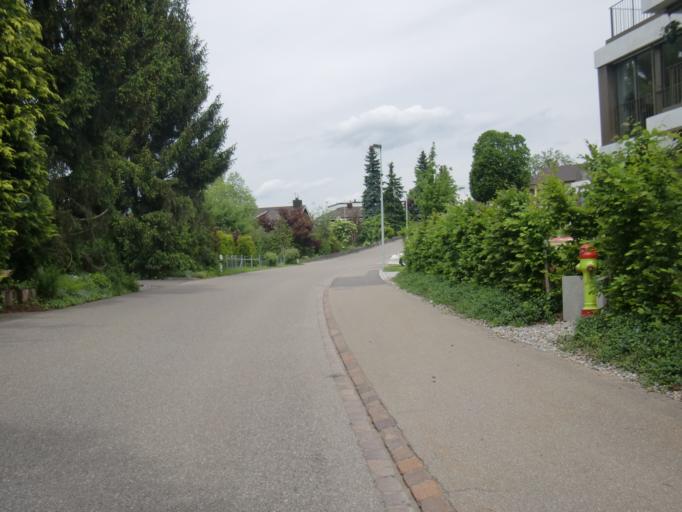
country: CH
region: Zurich
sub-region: Bezirk Hinwil
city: Hadlikon
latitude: 47.2864
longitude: 8.8580
